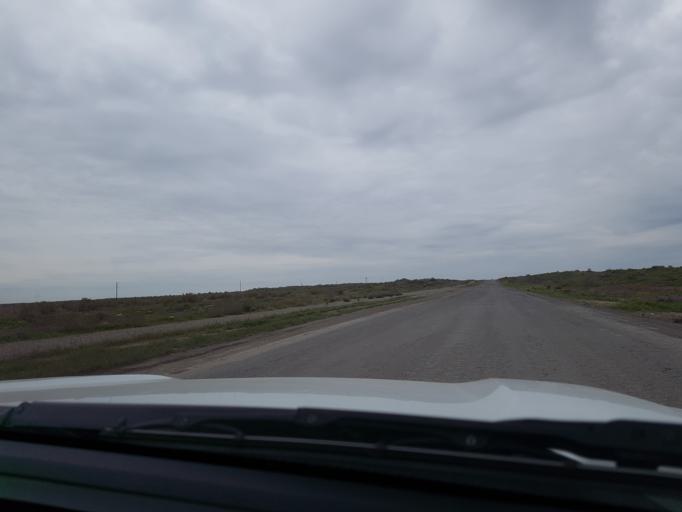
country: TM
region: Mary
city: Bayramaly
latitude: 37.9174
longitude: 62.6227
